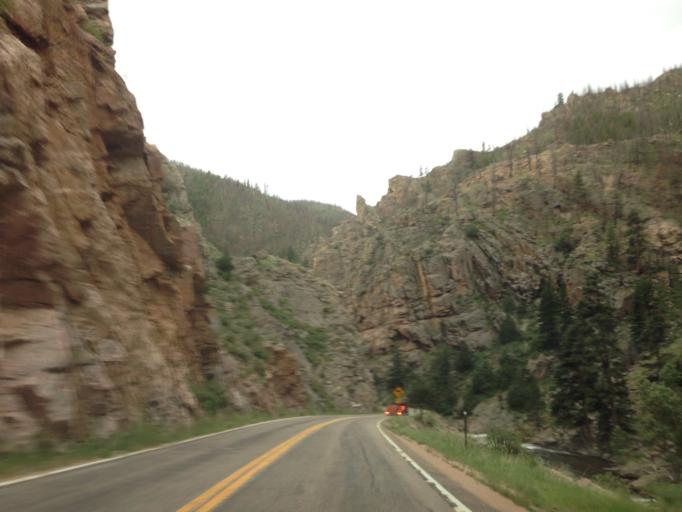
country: US
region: Colorado
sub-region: Larimer County
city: Laporte
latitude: 40.6769
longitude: -105.4298
